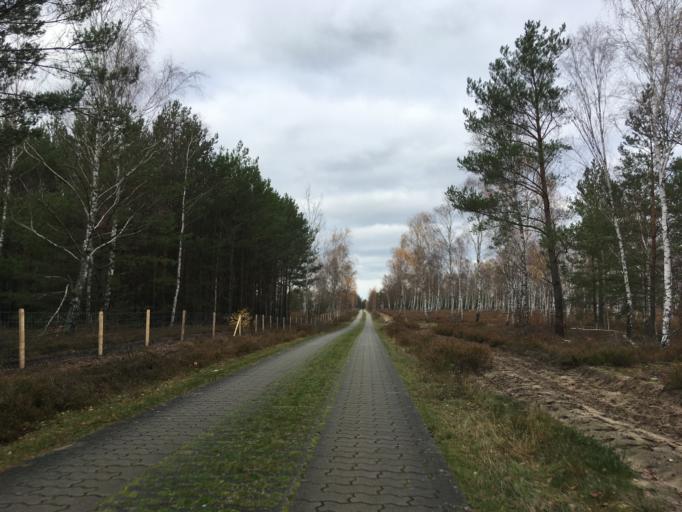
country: DE
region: Brandenburg
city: Tauer
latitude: 52.0023
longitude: 14.5050
